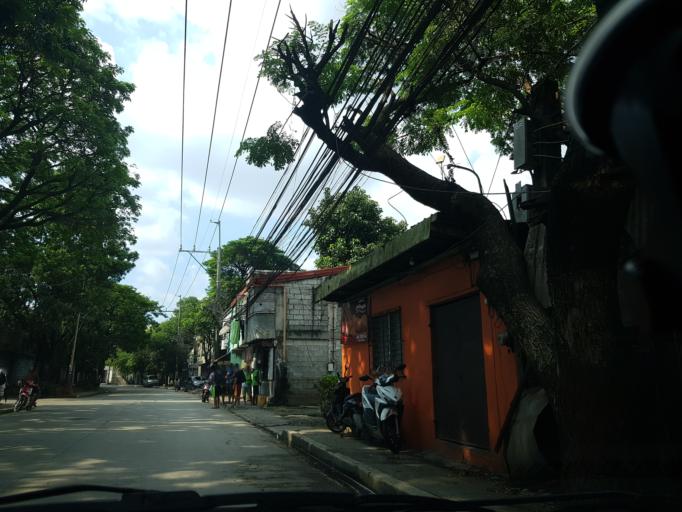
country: PH
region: Calabarzon
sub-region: Province of Rizal
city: Cainta
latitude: 14.5781
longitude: 121.0937
